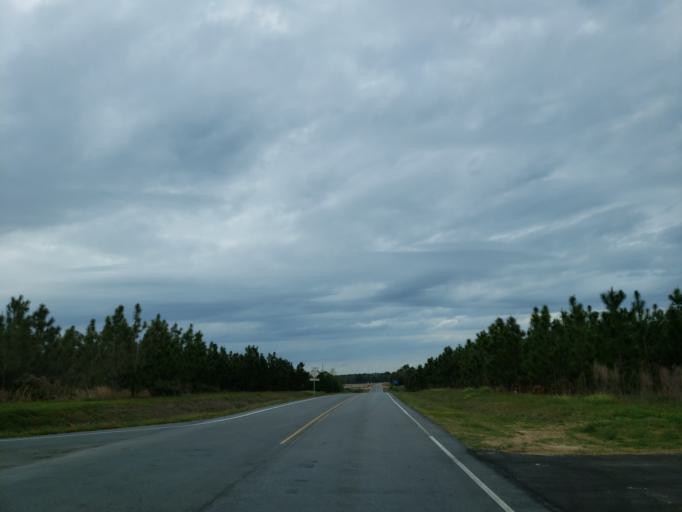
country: US
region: Georgia
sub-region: Dooly County
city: Vienna
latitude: 32.1193
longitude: -83.7561
